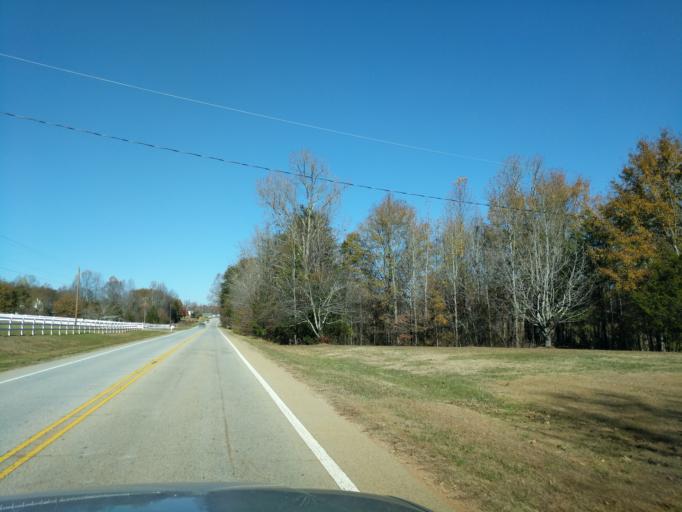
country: US
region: South Carolina
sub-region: Spartanburg County
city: Landrum
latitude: 35.1074
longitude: -82.2253
